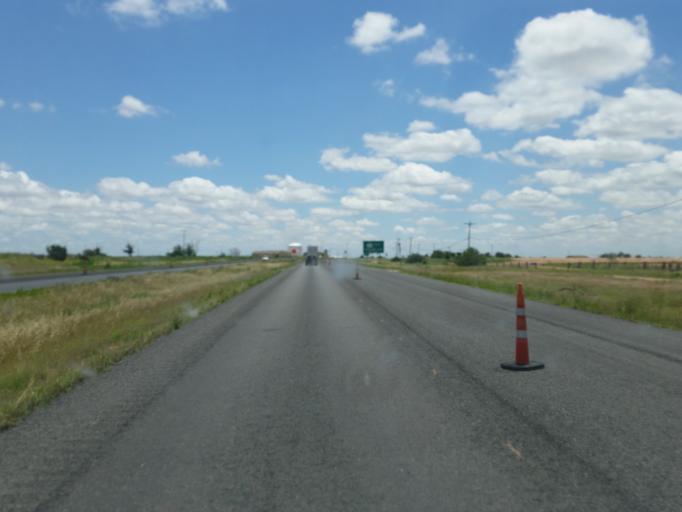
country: US
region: Texas
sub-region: Scurry County
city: Snyder
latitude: 32.7122
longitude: -100.8745
